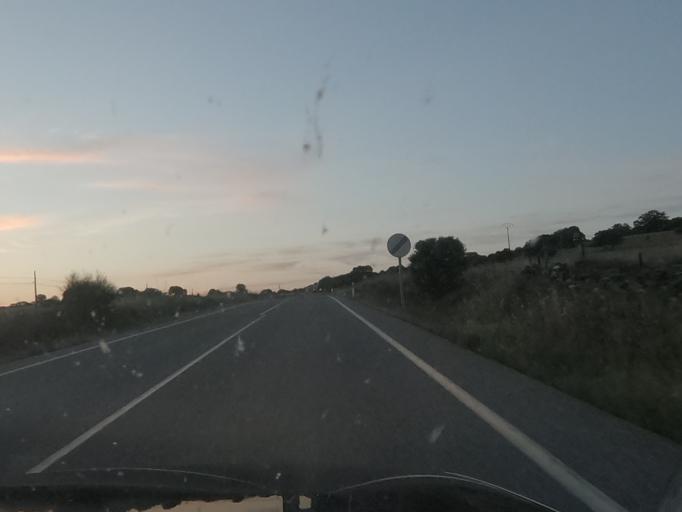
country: ES
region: Extremadura
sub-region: Provincia de Caceres
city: Piedras Albas
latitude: 39.7744
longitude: -6.9183
